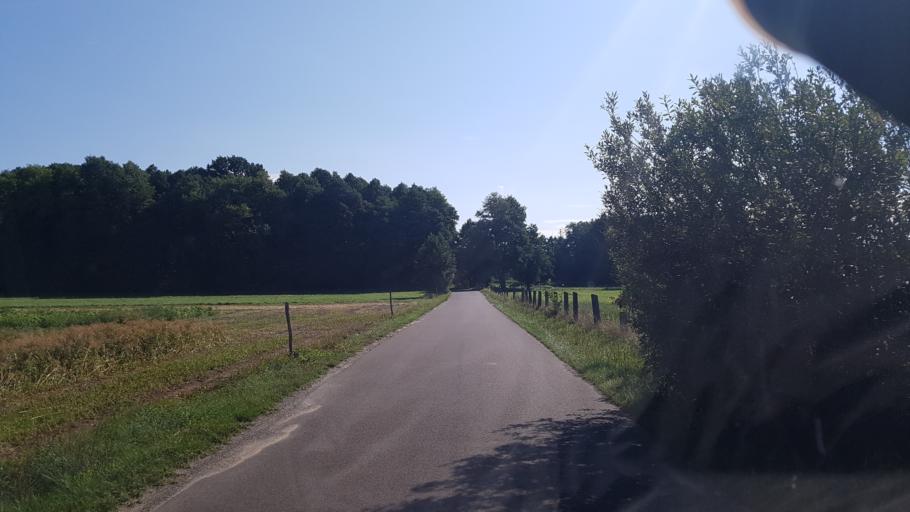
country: DE
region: Brandenburg
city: Vetschau
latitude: 51.7575
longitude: 14.0446
